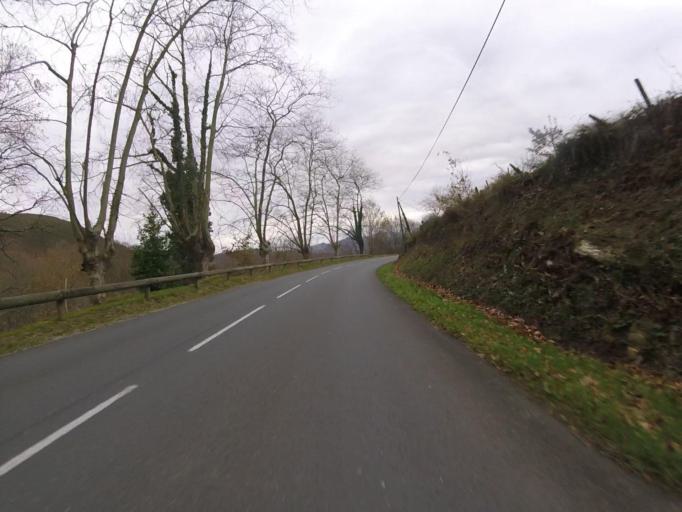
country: FR
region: Aquitaine
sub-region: Departement des Pyrenees-Atlantiques
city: Sare
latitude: 43.3219
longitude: -1.5988
